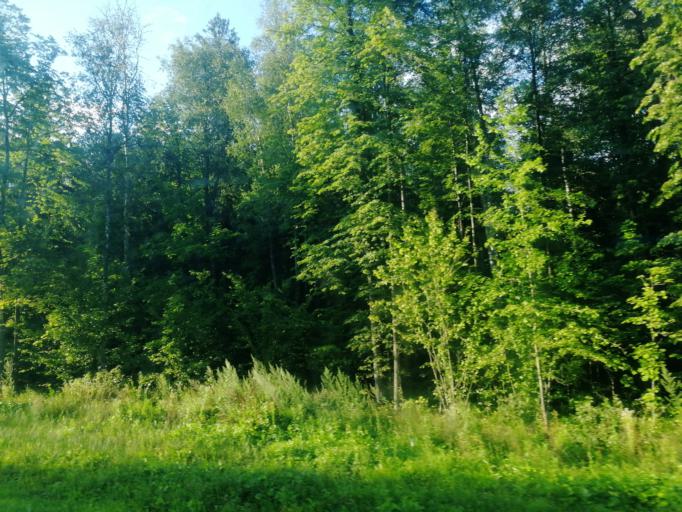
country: RU
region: Kaluga
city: Kaluga
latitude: 54.4466
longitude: 36.3127
